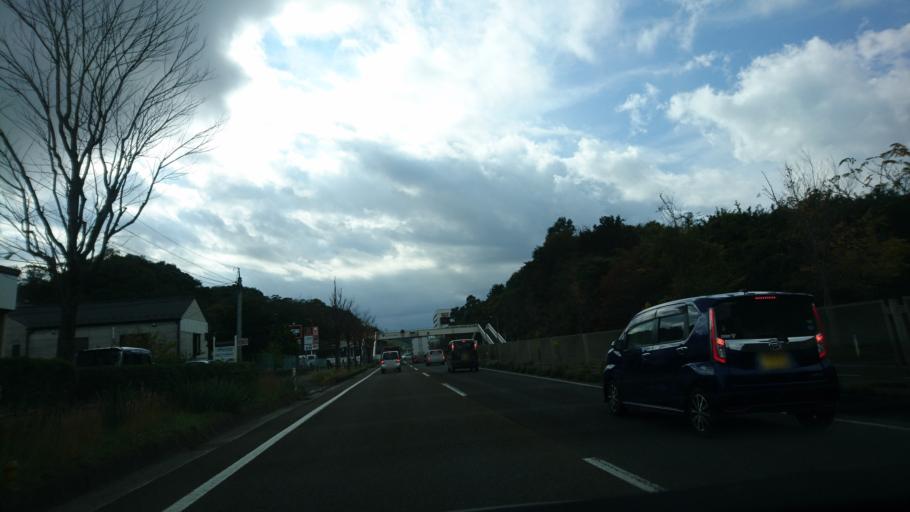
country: JP
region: Miyagi
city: Tomiya
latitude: 38.3746
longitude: 140.8740
